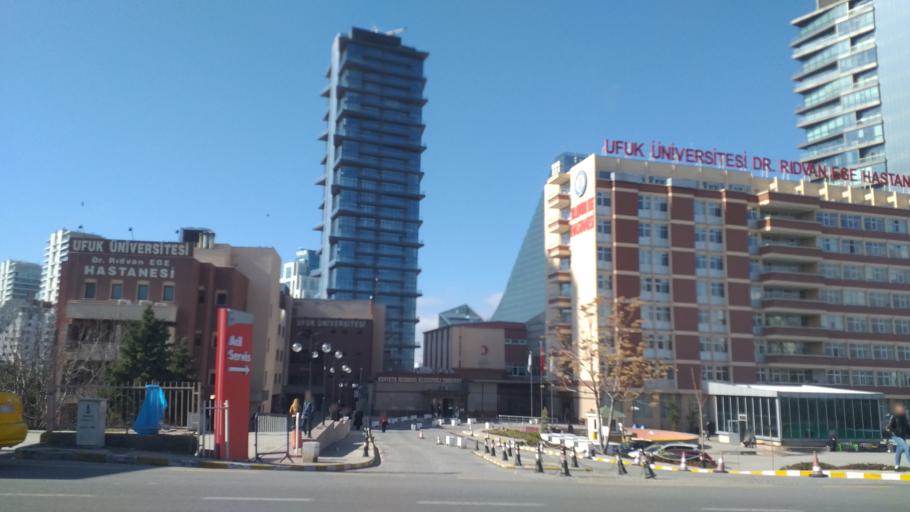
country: TR
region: Ankara
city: Ankara
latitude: 39.9100
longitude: 32.8146
